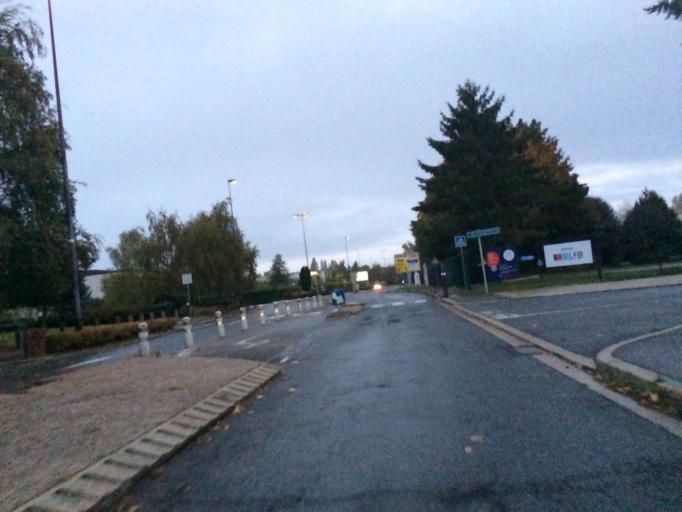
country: FR
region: Ile-de-France
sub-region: Departement de l'Essonne
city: Orsay
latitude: 48.6864
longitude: 2.1948
